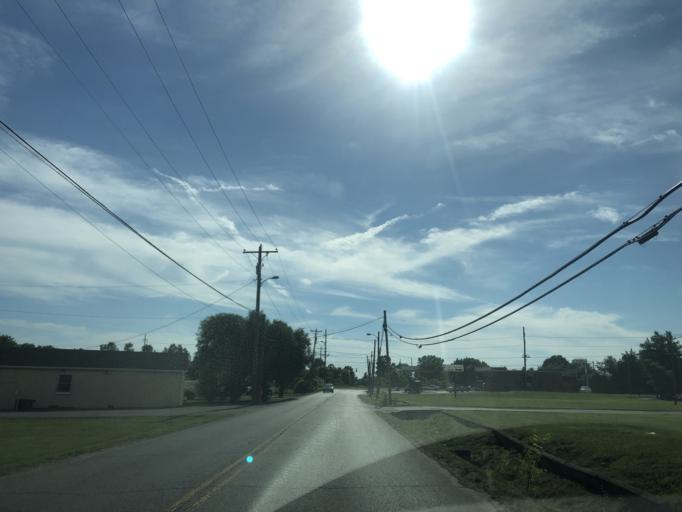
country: US
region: Tennessee
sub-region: Davidson County
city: Nashville
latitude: 36.2075
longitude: -86.8378
